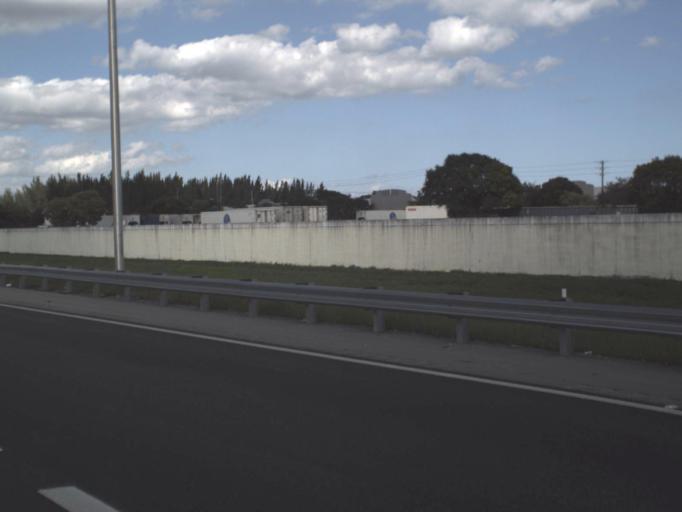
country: US
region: Florida
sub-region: Broward County
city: Davie
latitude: 26.0701
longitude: -80.2154
